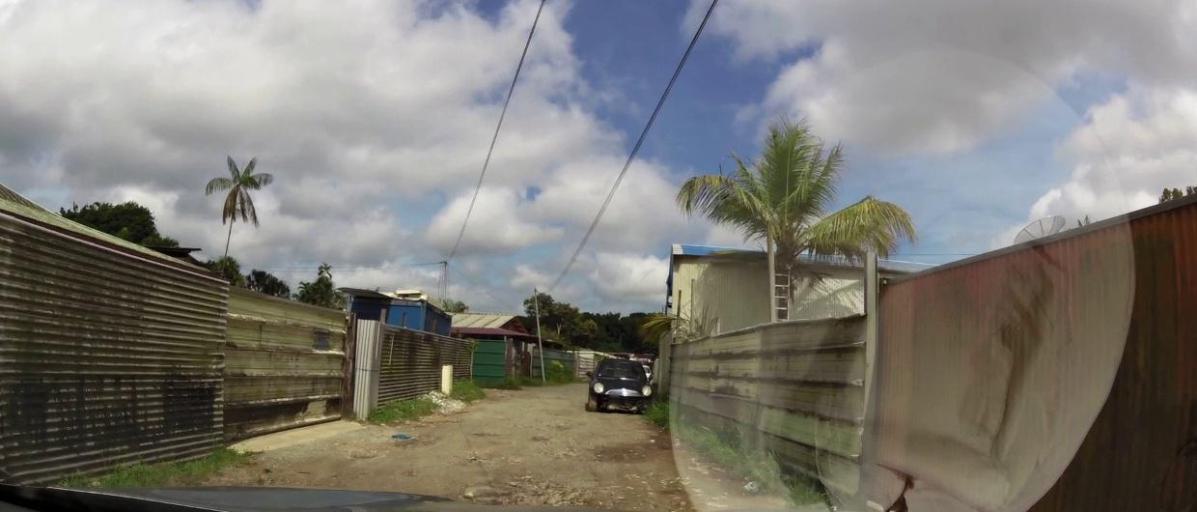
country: GF
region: Guyane
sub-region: Guyane
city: Matoury
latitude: 4.8769
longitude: -52.3277
